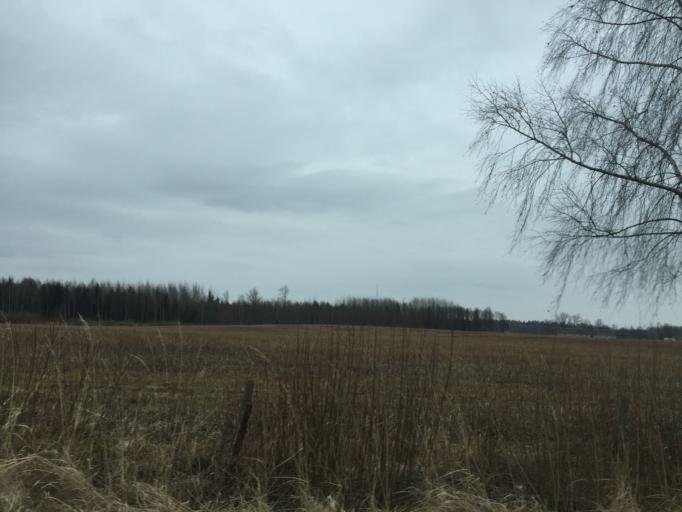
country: LV
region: Lielvarde
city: Lielvarde
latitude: 56.7577
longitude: 24.8323
